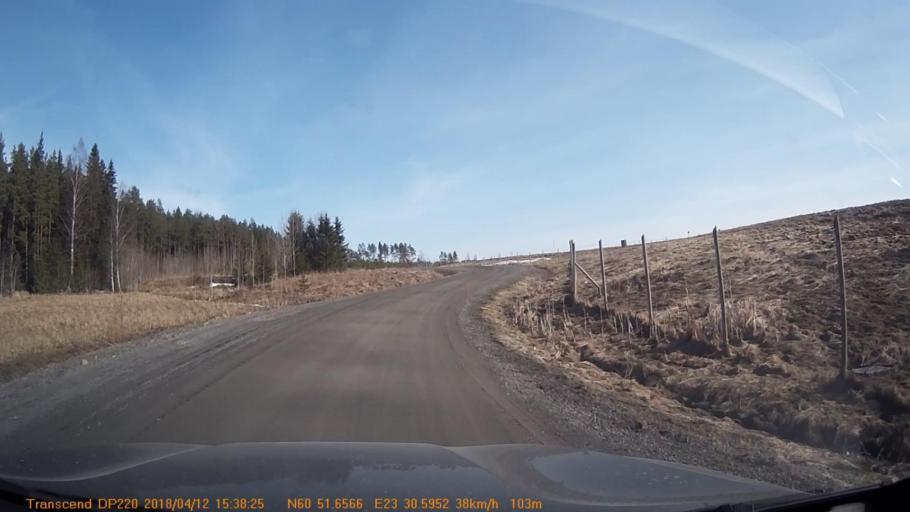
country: FI
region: Haeme
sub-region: Forssa
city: Jokioinen
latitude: 60.8606
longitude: 23.5107
